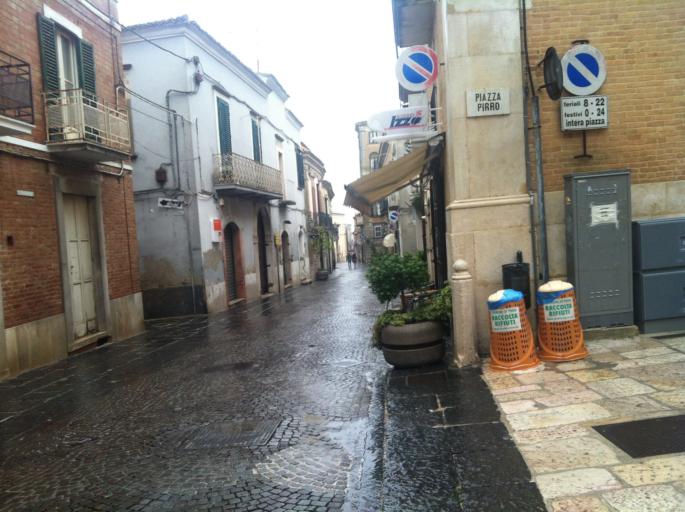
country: IT
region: Apulia
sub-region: Provincia di Foggia
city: Troia
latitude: 41.3613
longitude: 15.3085
